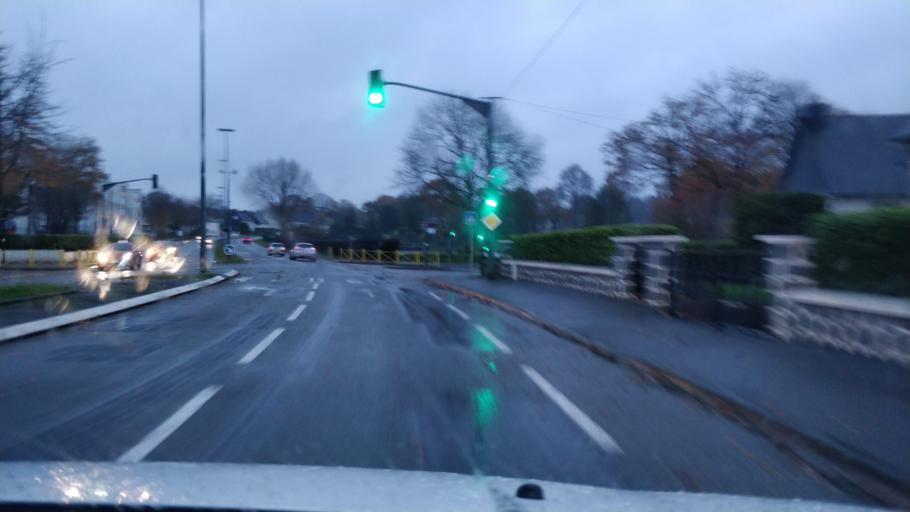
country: FR
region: Brittany
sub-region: Departement des Cotes-d'Armor
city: Loudeac
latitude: 48.1780
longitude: -2.7478
